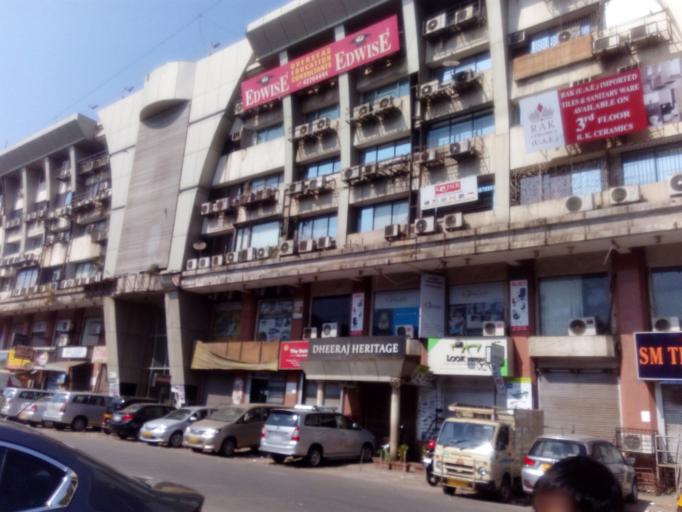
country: IN
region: Maharashtra
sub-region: Mumbai Suburban
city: Mumbai
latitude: 19.0898
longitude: 72.8377
